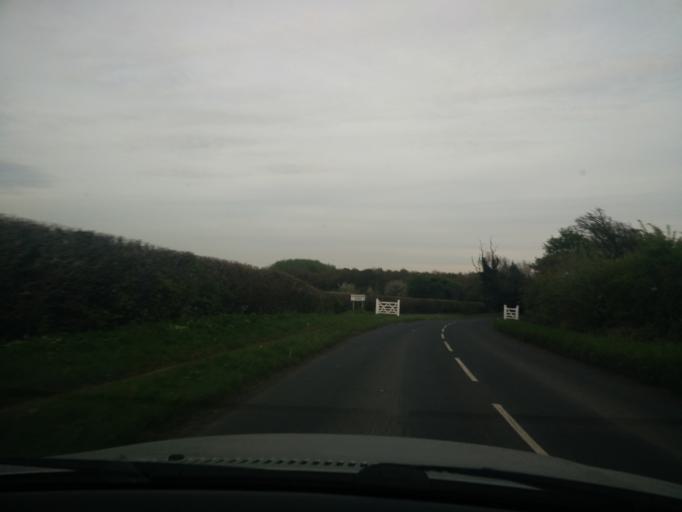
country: GB
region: England
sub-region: Buckinghamshire
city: Amersham on the Hill
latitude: 51.6880
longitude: -0.6256
